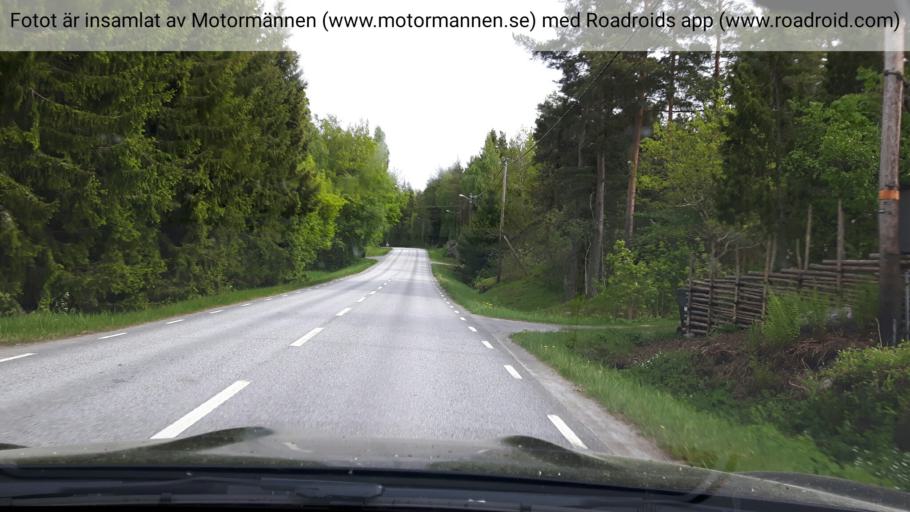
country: SE
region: Stockholm
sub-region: Norrtalje Kommun
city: Norrtalje
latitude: 59.6757
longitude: 18.7659
